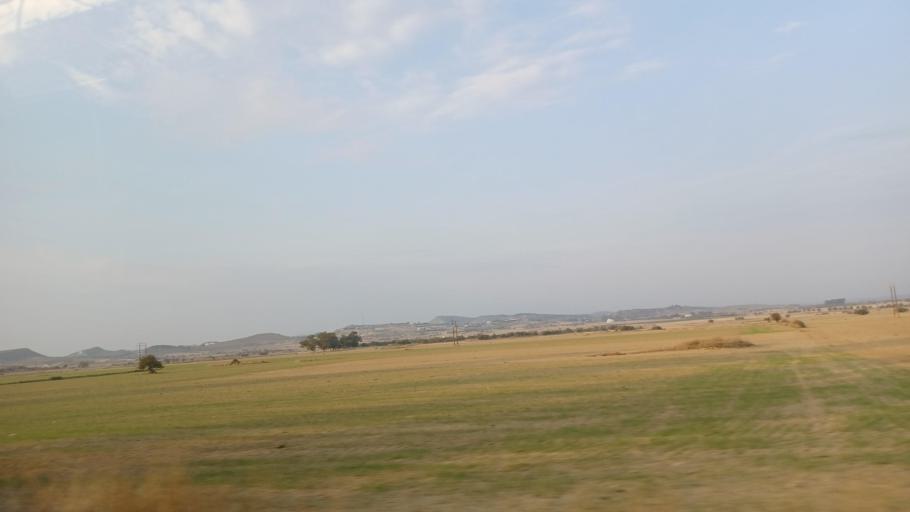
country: CY
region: Lefkosia
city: Lympia
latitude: 35.0279
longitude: 33.4930
